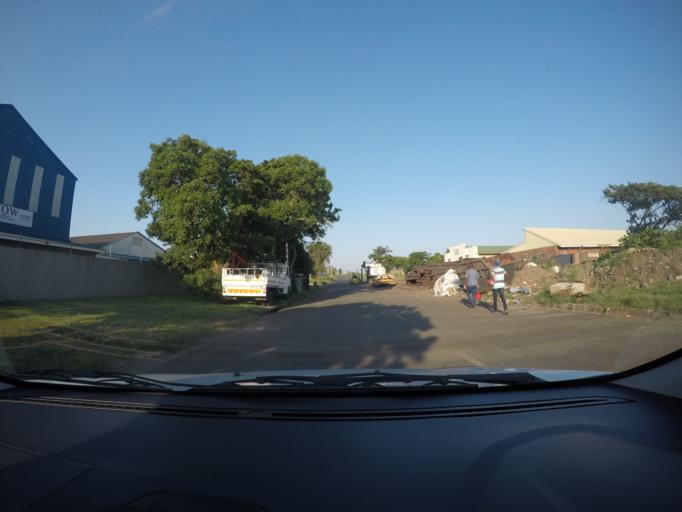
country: ZA
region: KwaZulu-Natal
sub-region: uThungulu District Municipality
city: Richards Bay
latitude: -28.7643
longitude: 32.0062
